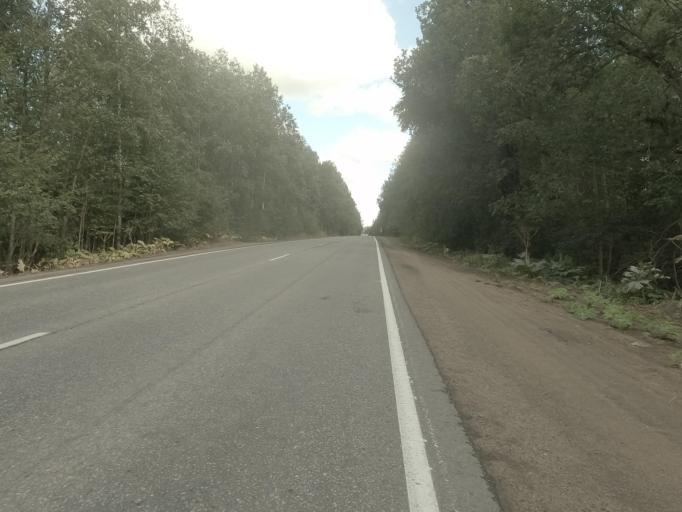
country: RU
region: Leningrad
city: Shcheglovo
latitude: 60.0199
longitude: 30.7362
